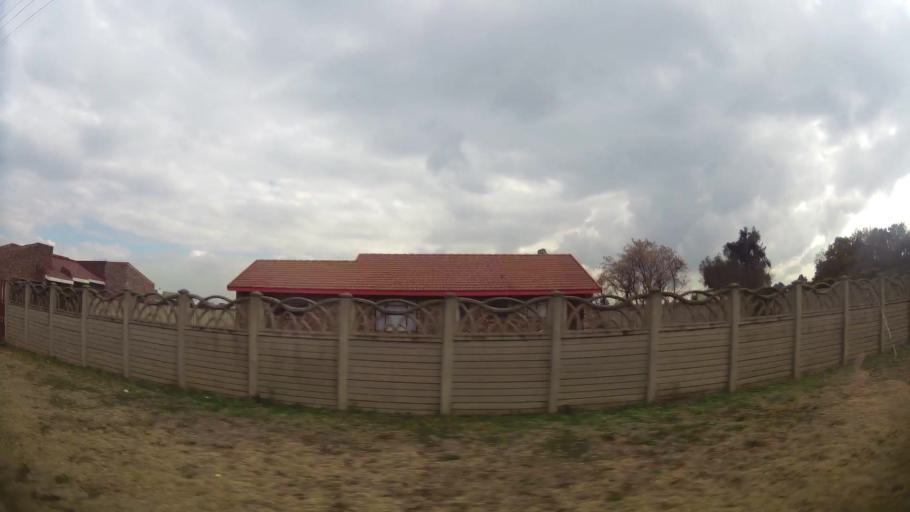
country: ZA
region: Gauteng
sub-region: Sedibeng District Municipality
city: Meyerton
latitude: -26.5869
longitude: 27.9998
